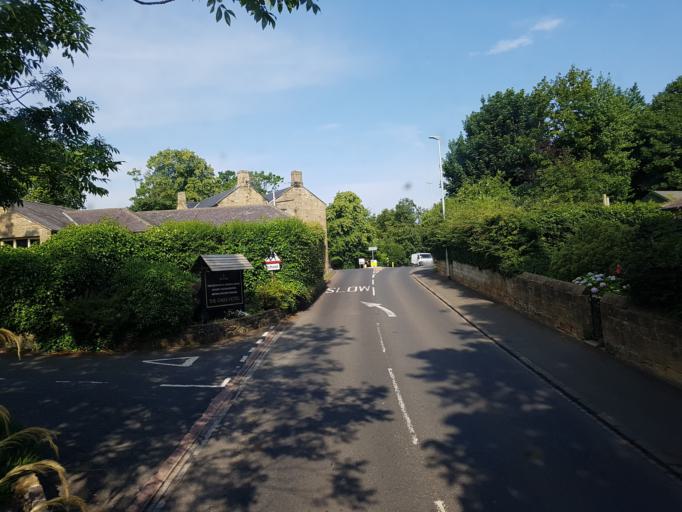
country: GB
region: England
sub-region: Northumberland
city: Alnwick
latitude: 55.4083
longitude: -1.6929
